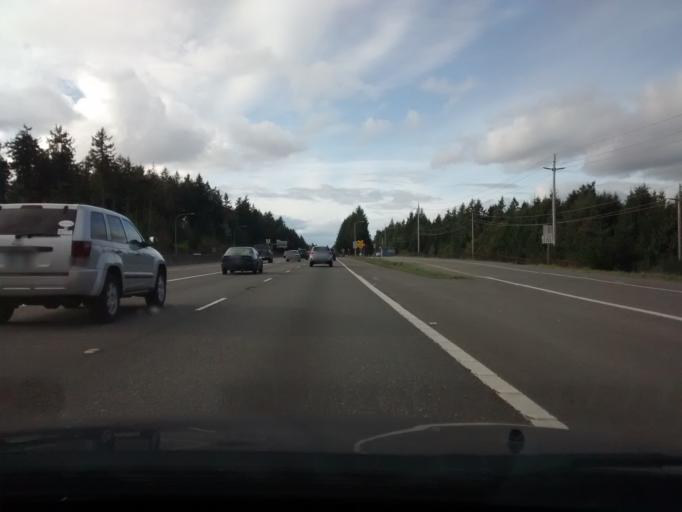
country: US
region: Washington
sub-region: Pierce County
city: Wollochet
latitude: 47.2920
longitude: -122.5645
